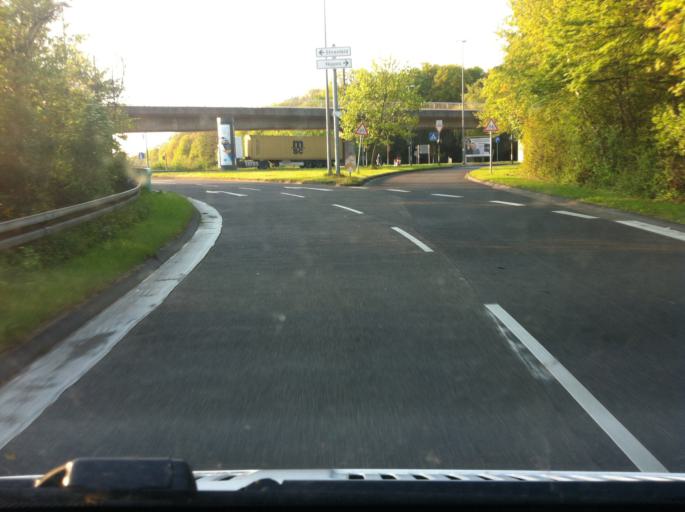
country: DE
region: North Rhine-Westphalia
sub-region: Regierungsbezirk Koln
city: Neuehrenfeld
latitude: 50.9592
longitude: 6.9287
